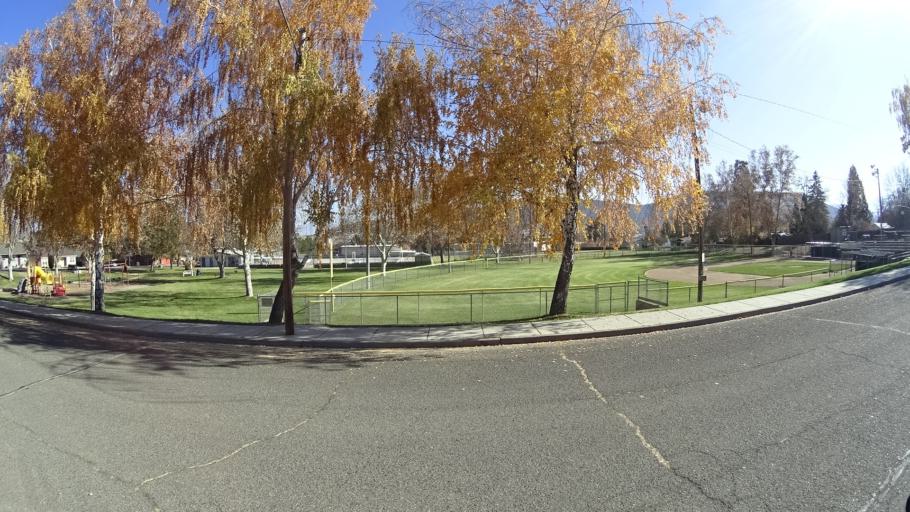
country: US
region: California
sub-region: Siskiyou County
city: Yreka
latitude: 41.7389
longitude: -122.6411
